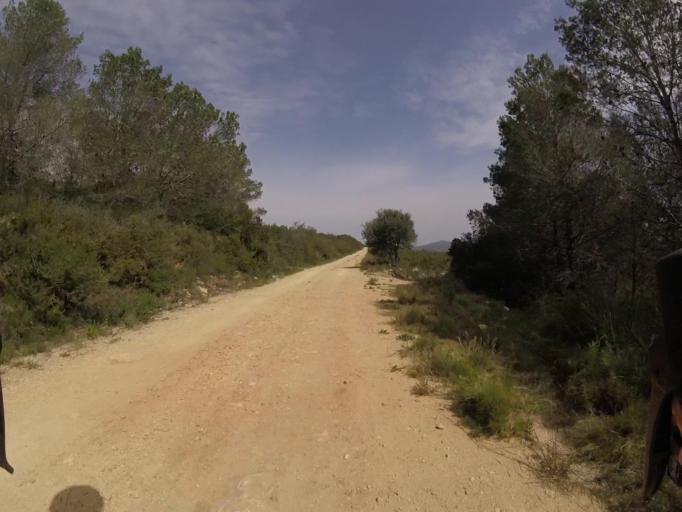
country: ES
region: Valencia
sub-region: Provincia de Castello
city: Cuevas de Vinroma
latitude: 40.2896
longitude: 0.1210
